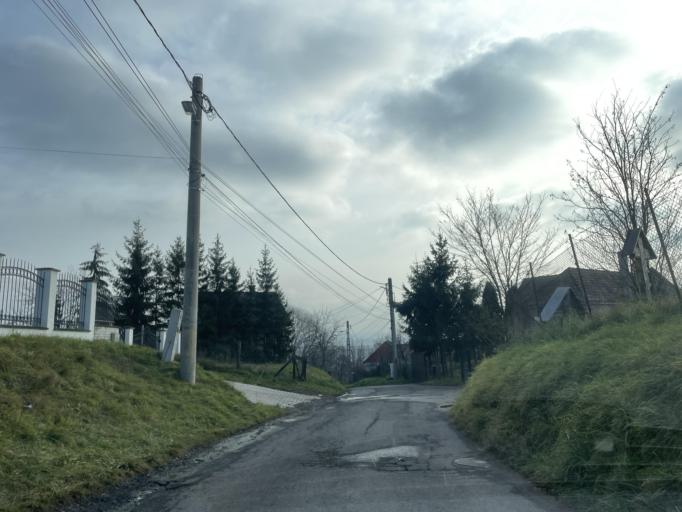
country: RO
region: Mures
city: Reghin-Sat
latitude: 46.7900
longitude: 24.7101
